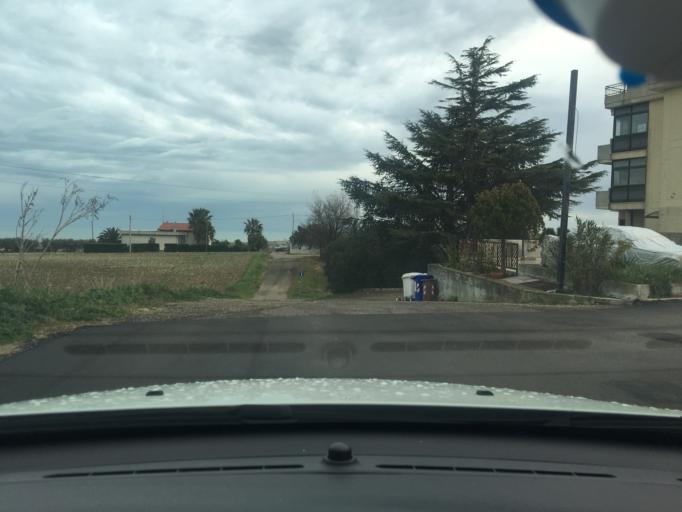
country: IT
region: Molise
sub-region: Provincia di Campobasso
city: Termoli
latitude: 41.9746
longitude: 14.9957
